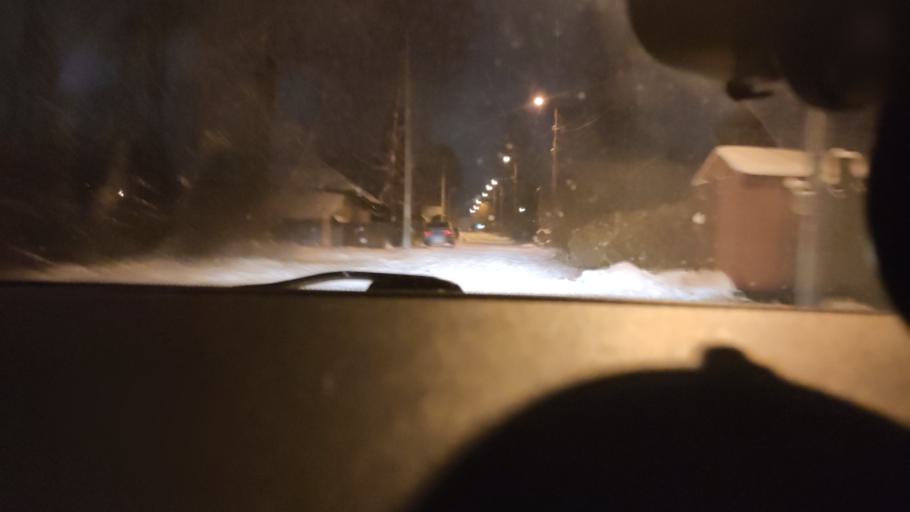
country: RU
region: Perm
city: Perm
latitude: 58.0299
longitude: 56.2220
